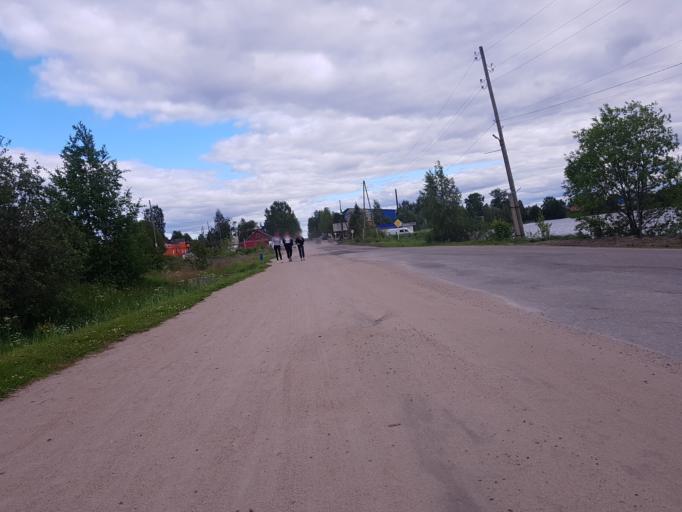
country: RU
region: Republic of Karelia
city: Kalevala
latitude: 65.1997
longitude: 31.1785
